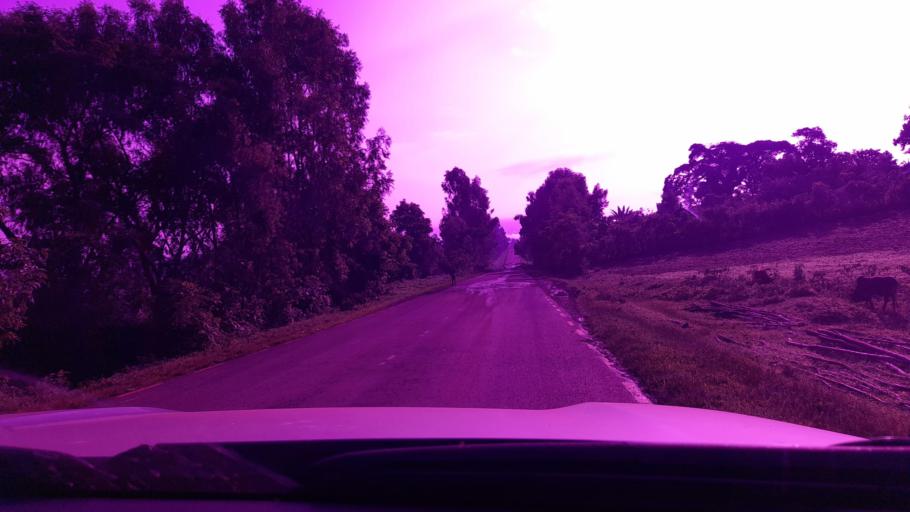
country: ET
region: Oromiya
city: Bedele
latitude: 8.1508
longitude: 36.4657
